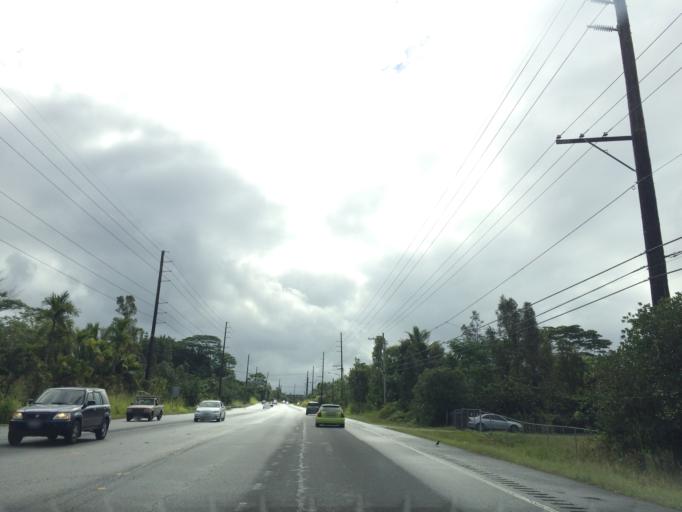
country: US
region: Hawaii
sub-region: Hawaii County
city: Ainaloa
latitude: 19.5478
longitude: -154.9798
